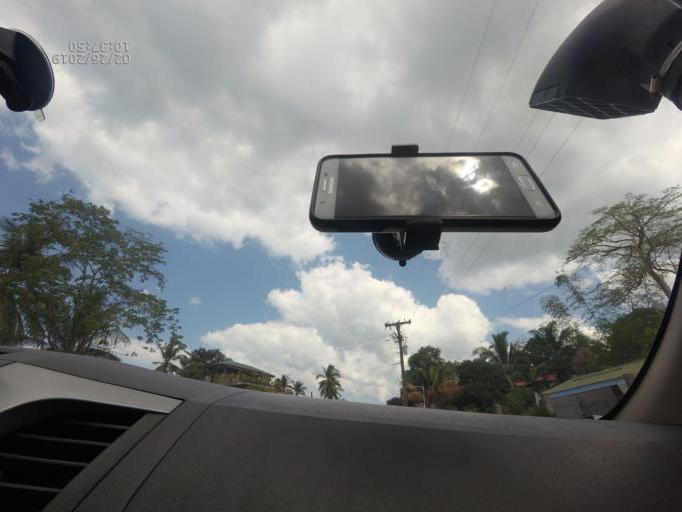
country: PH
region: Mimaropa
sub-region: Province of Palawan
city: Salvacion
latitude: 12.1307
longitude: 119.9373
